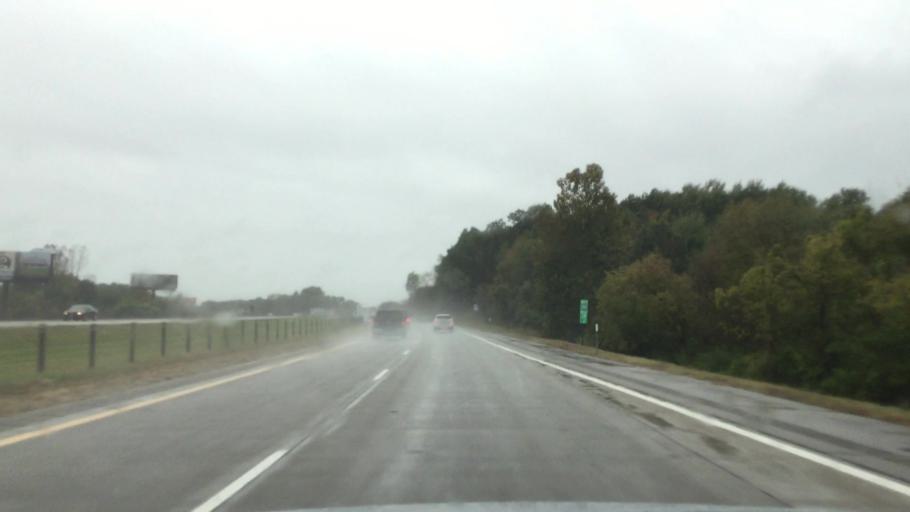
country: US
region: Michigan
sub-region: Berrien County
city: Coloma
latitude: 42.1750
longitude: -86.3114
